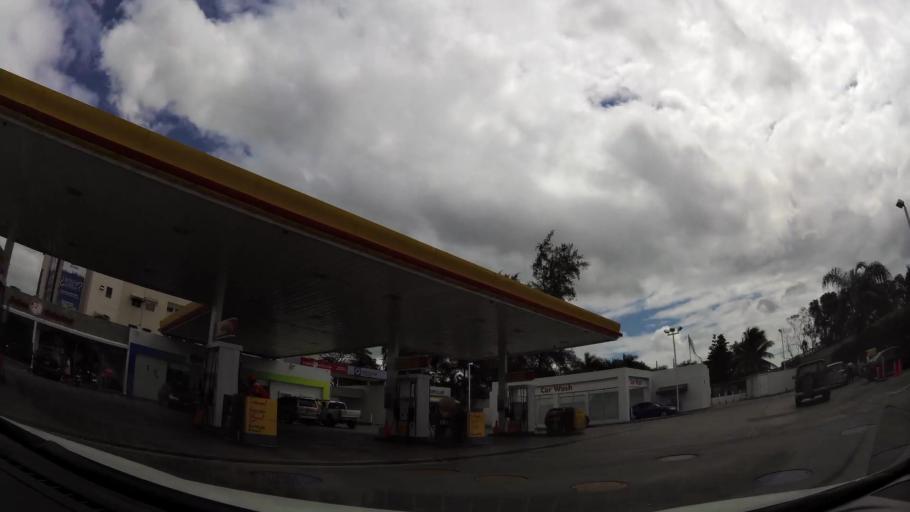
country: DO
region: Nacional
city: Bella Vista
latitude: 18.4689
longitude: -69.9681
